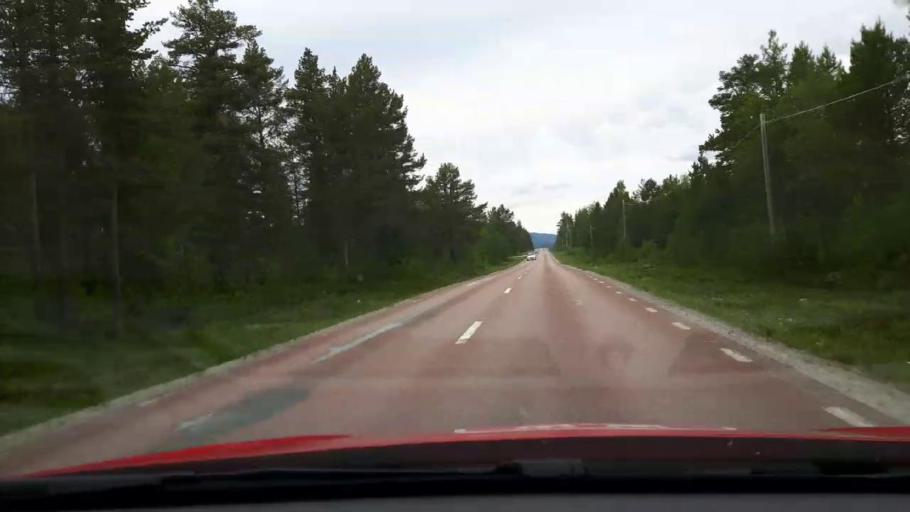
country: NO
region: Hedmark
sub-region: Engerdal
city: Engerdal
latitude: 62.4951
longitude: 12.6348
